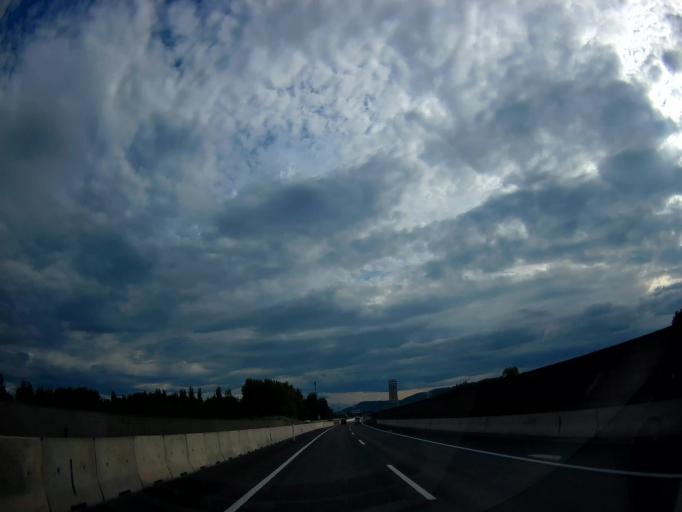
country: AT
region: Lower Austria
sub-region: Politischer Bezirk Krems
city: Grafenegg
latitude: 48.4014
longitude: 15.7380
